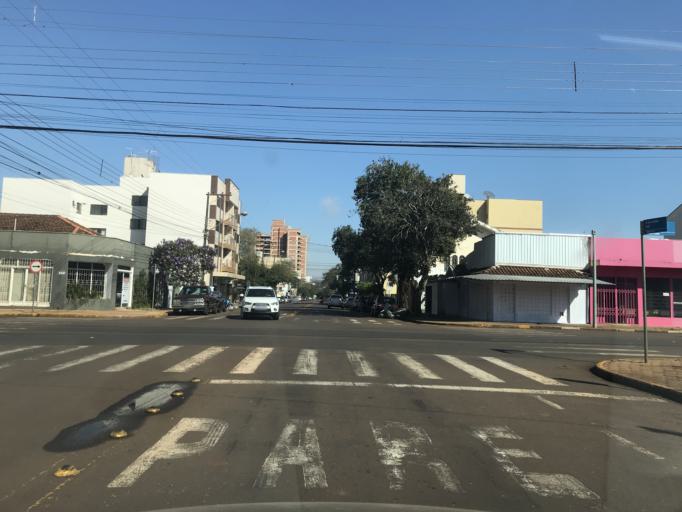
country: BR
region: Parana
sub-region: Toledo
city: Toledo
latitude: -24.7238
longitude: -53.7370
